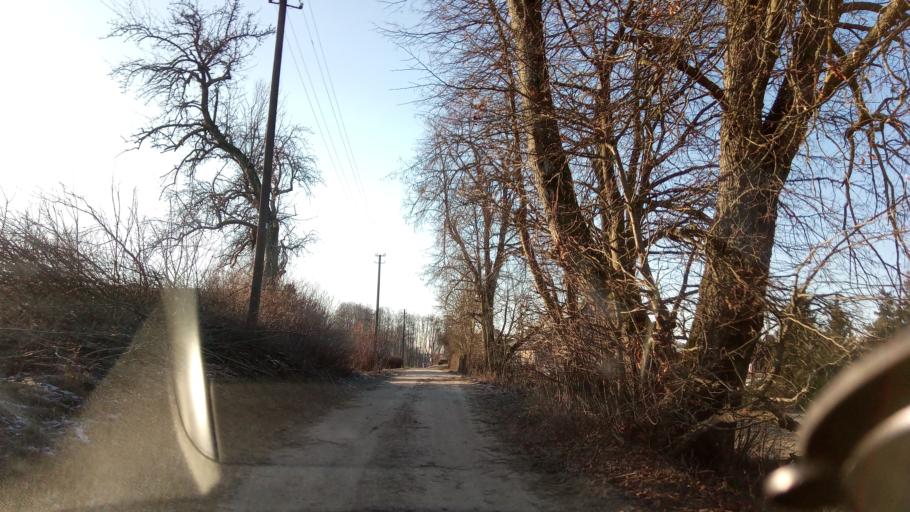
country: LT
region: Alytaus apskritis
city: Druskininkai
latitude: 54.1007
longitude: 24.0145
